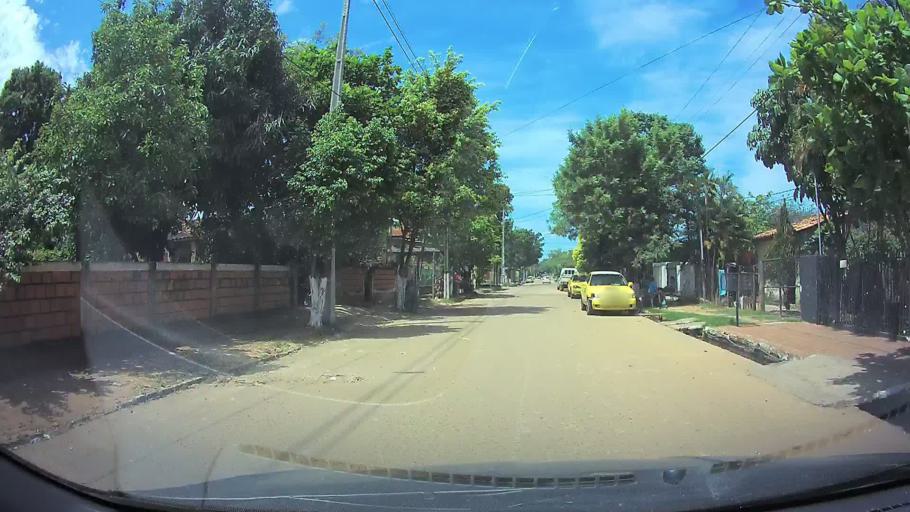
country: PY
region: Central
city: Limpio
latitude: -25.1718
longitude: -57.4761
